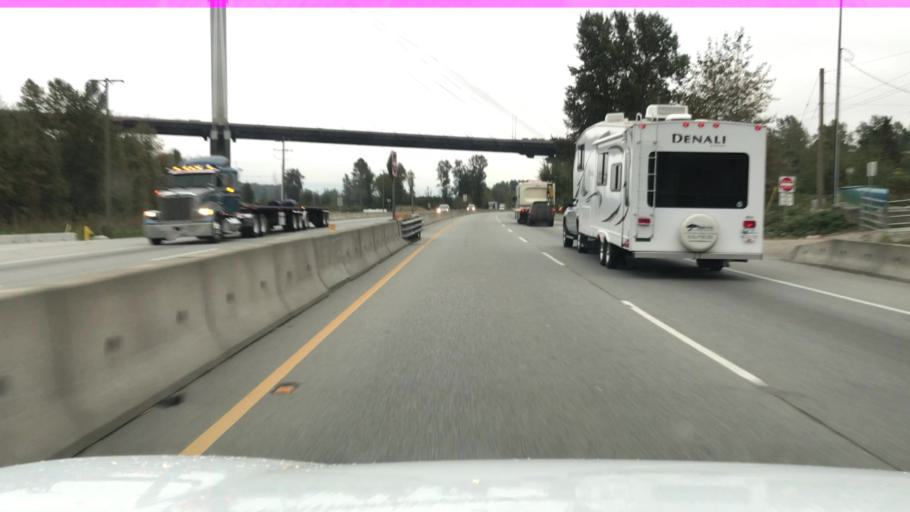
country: CA
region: British Columbia
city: Port Moody
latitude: 49.2146
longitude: -122.8176
